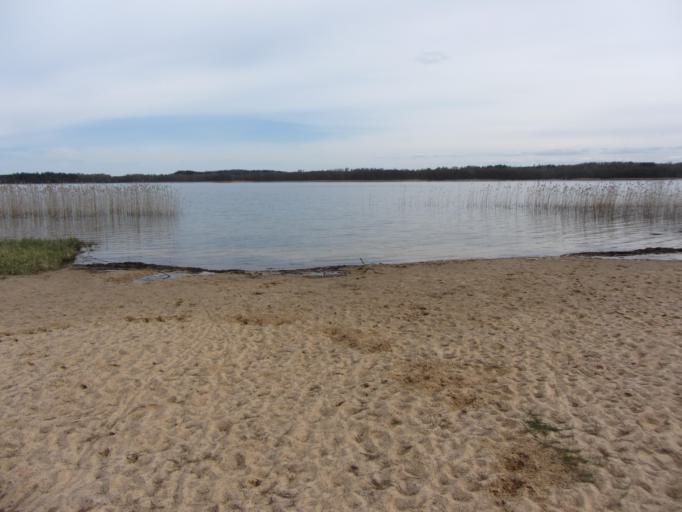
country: LT
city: Zarasai
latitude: 55.5815
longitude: 26.1567
